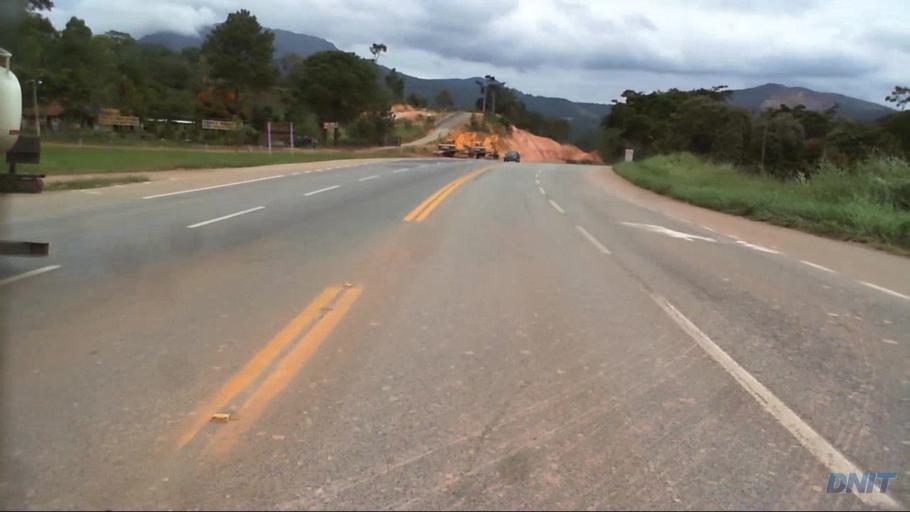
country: BR
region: Minas Gerais
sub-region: Caete
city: Caete
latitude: -19.7754
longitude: -43.6523
